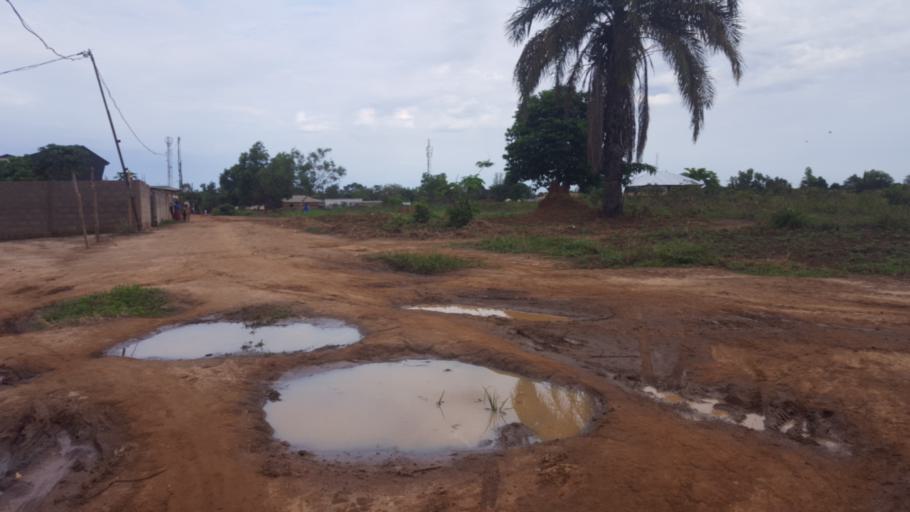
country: CD
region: Bandundu
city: Bandundu
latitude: -3.3020
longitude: 17.3783
